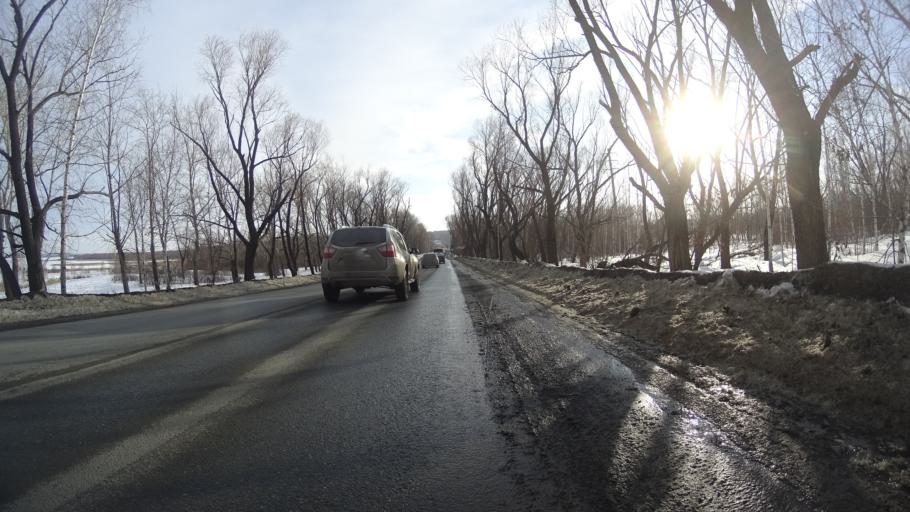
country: RU
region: Chelyabinsk
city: Sargazy
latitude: 55.1439
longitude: 61.2837
